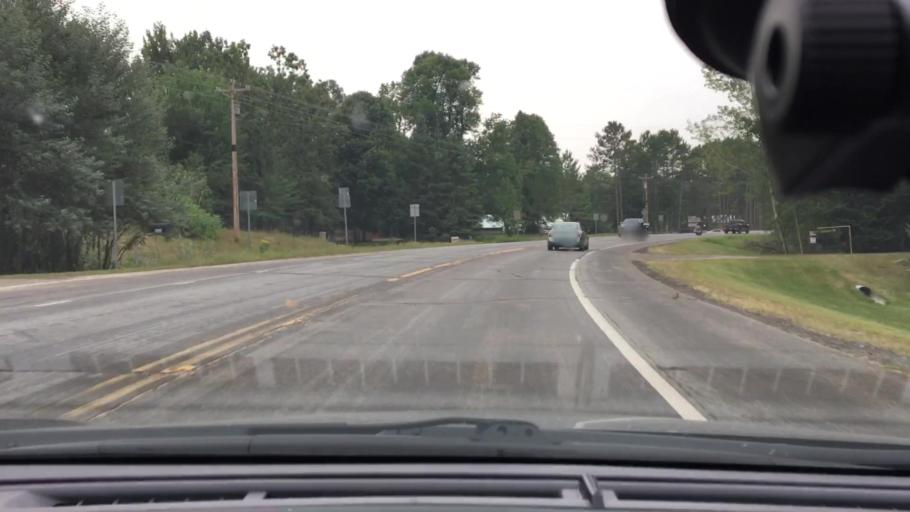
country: US
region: Minnesota
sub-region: Crow Wing County
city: Cross Lake
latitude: 46.8172
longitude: -93.9426
